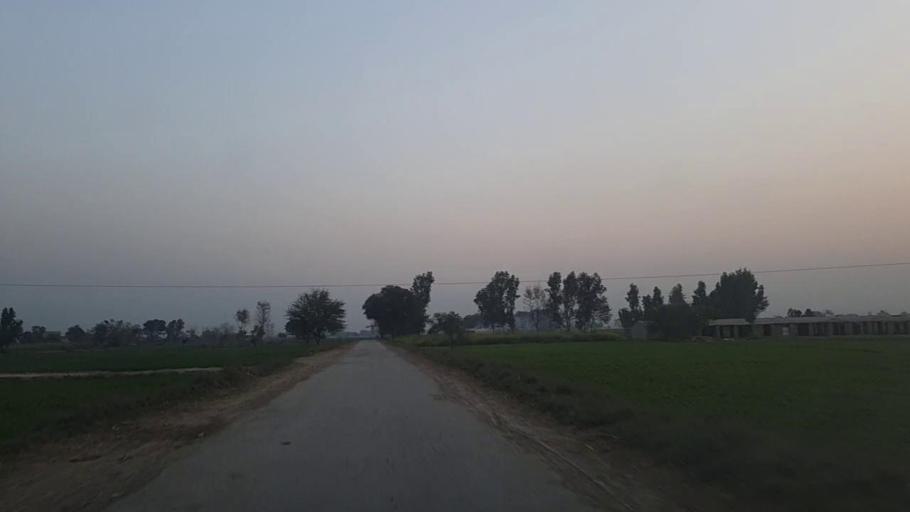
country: PK
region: Sindh
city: Naushahro Firoz
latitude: 26.8660
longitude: 68.0473
